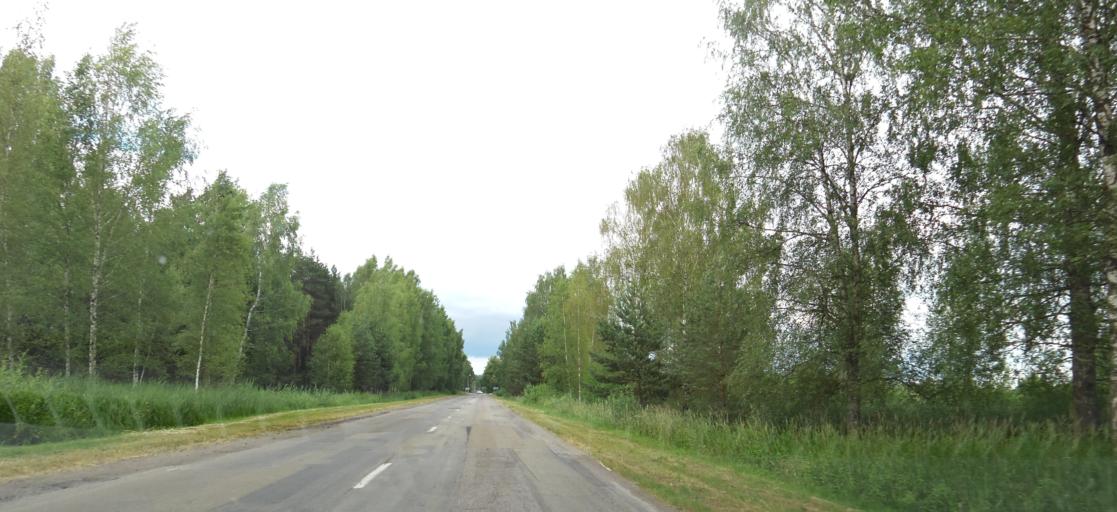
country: LT
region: Panevezys
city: Pasvalys
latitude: 56.0469
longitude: 24.3811
